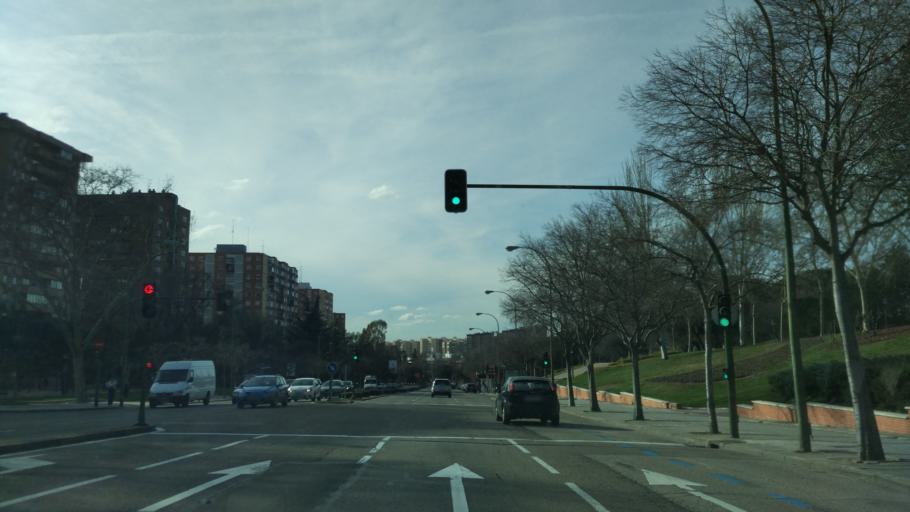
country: ES
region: Madrid
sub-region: Provincia de Madrid
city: Tetuan de las Victorias
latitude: 40.4796
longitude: -3.6962
